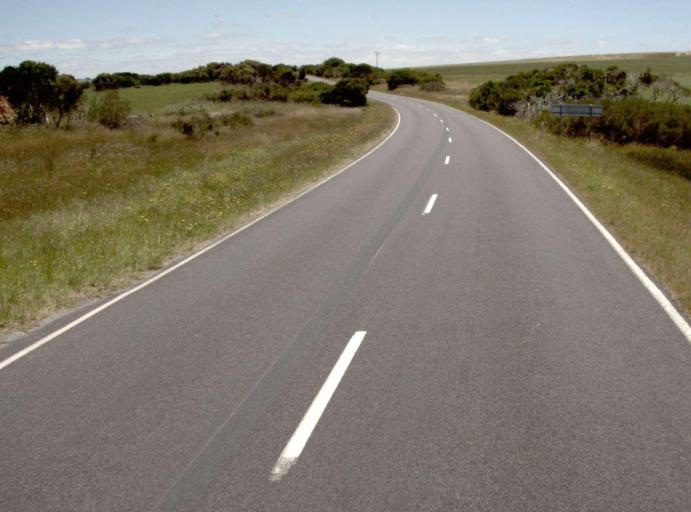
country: AU
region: Victoria
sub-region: Latrobe
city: Morwell
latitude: -38.8306
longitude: 146.2387
